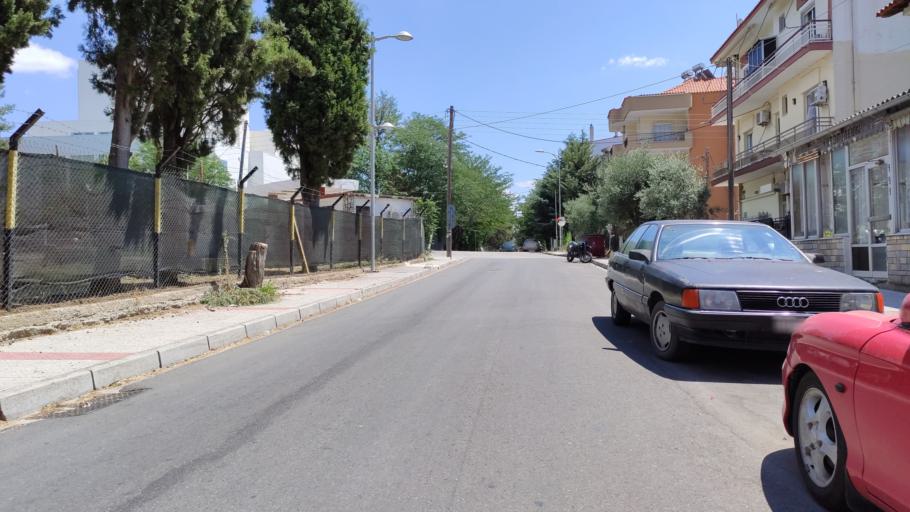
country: GR
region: East Macedonia and Thrace
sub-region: Nomos Rodopis
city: Komotini
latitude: 41.1291
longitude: 25.4094
